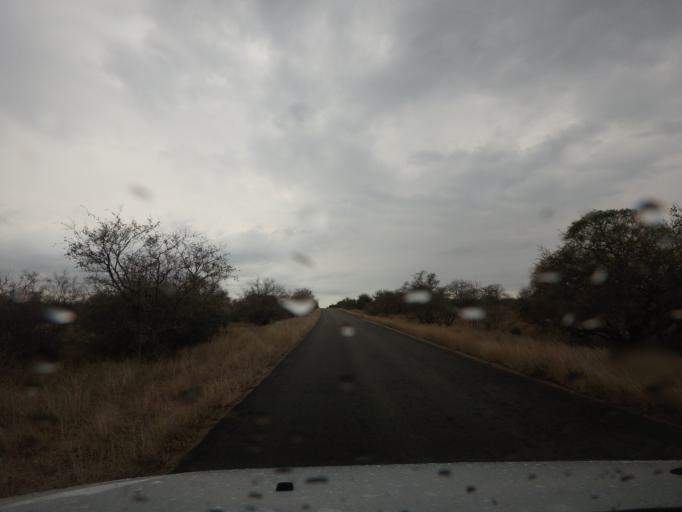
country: ZA
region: Limpopo
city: Thulamahashi
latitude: -24.4721
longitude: 31.4281
